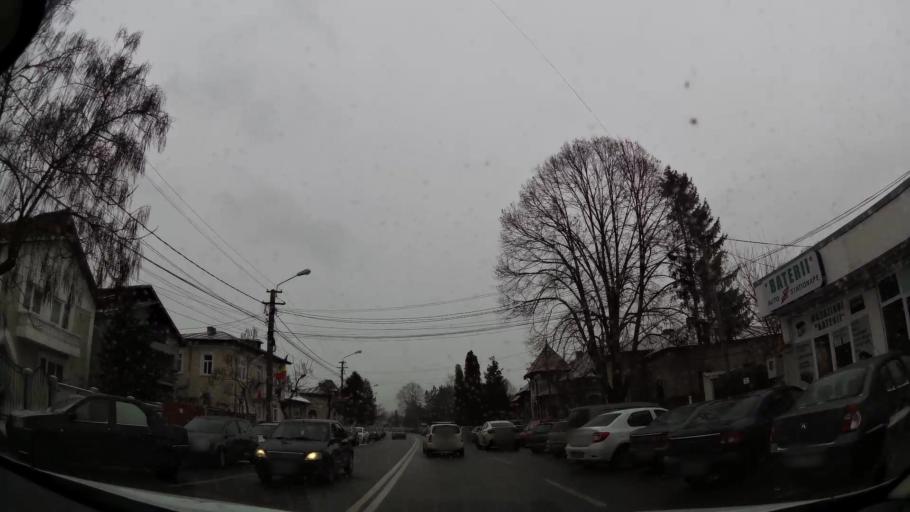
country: RO
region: Dambovita
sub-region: Municipiul Targoviste
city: Targoviste
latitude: 44.9345
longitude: 25.4534
